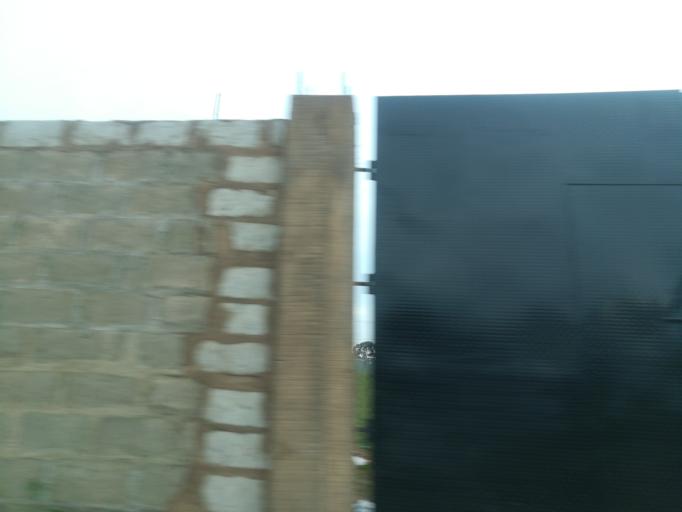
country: NG
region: Oyo
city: Ibadan
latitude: 7.4422
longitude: 3.9074
